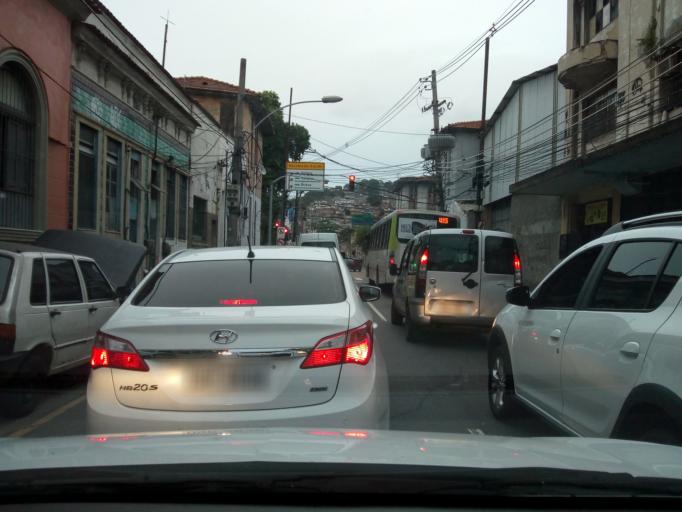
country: BR
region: Rio de Janeiro
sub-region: Rio De Janeiro
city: Rio de Janeiro
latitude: -22.9120
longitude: -43.1994
